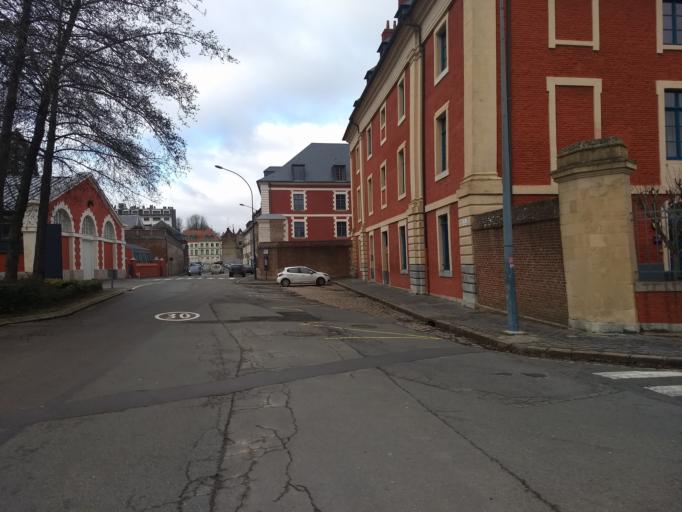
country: FR
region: Nord-Pas-de-Calais
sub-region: Departement du Pas-de-Calais
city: Achicourt
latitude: 50.2890
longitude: 2.7651
